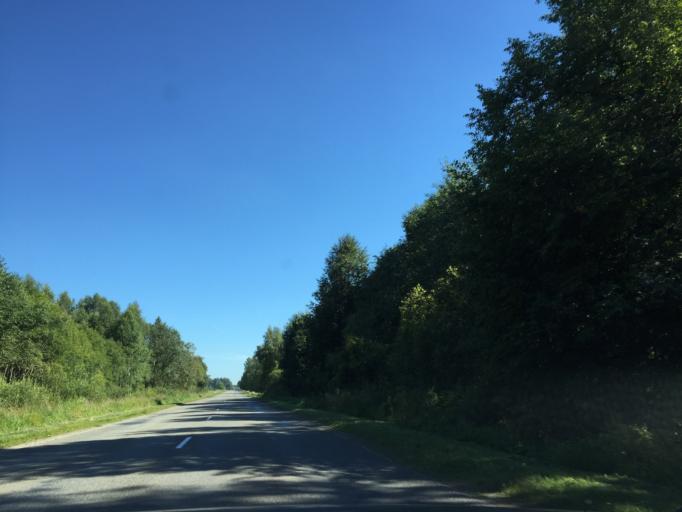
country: LV
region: Akniste
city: Akniste
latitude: 56.1511
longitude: 25.7770
